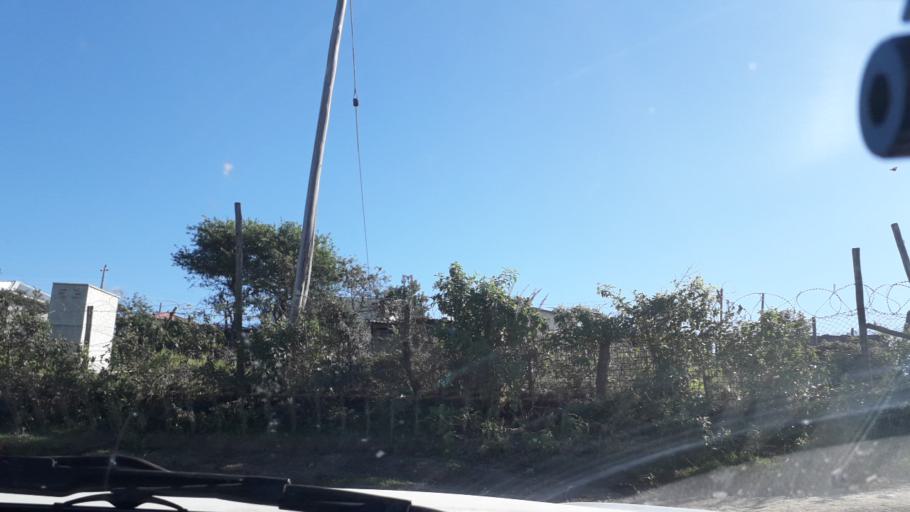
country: ZA
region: Eastern Cape
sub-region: Buffalo City Metropolitan Municipality
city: East London
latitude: -32.7996
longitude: 27.9618
